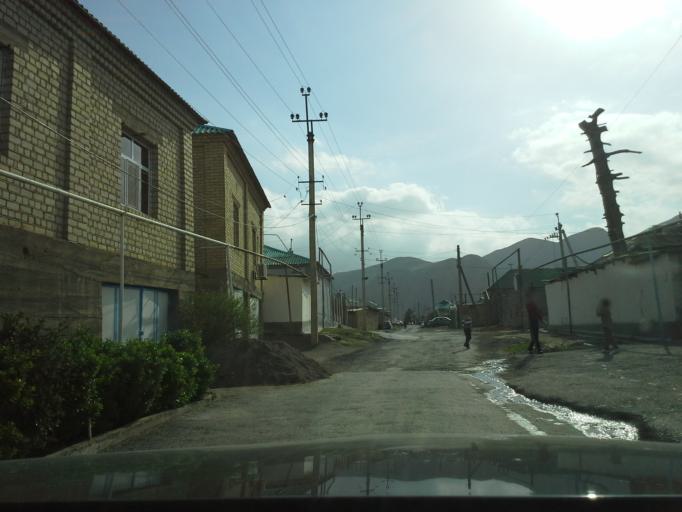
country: TM
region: Ahal
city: Abadan
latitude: 37.9555
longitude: 58.2090
